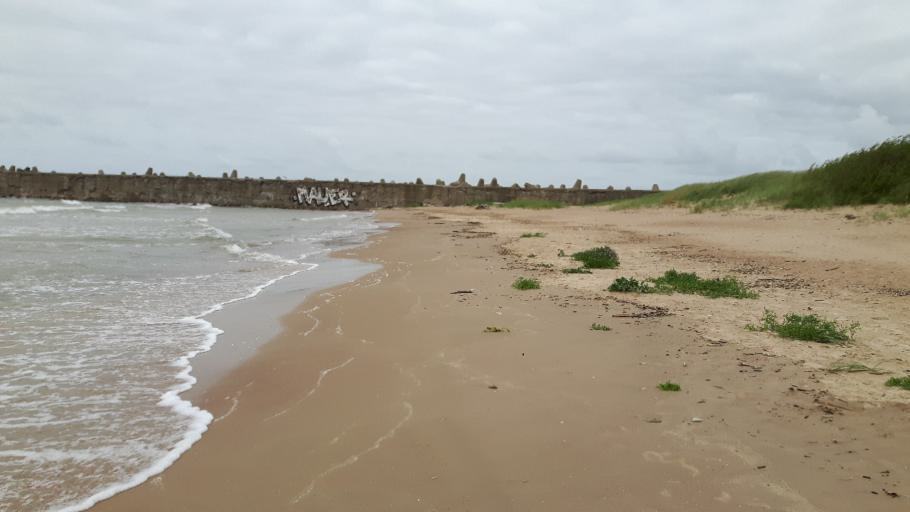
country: LV
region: Liepaja
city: Vec-Liepaja
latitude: 56.5564
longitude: 20.9977
